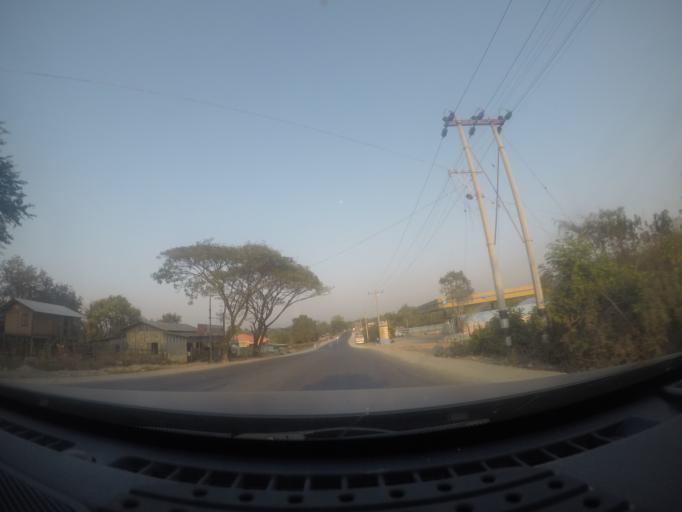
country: MM
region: Mandalay
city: Yamethin
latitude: 20.7550
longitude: 96.3075
